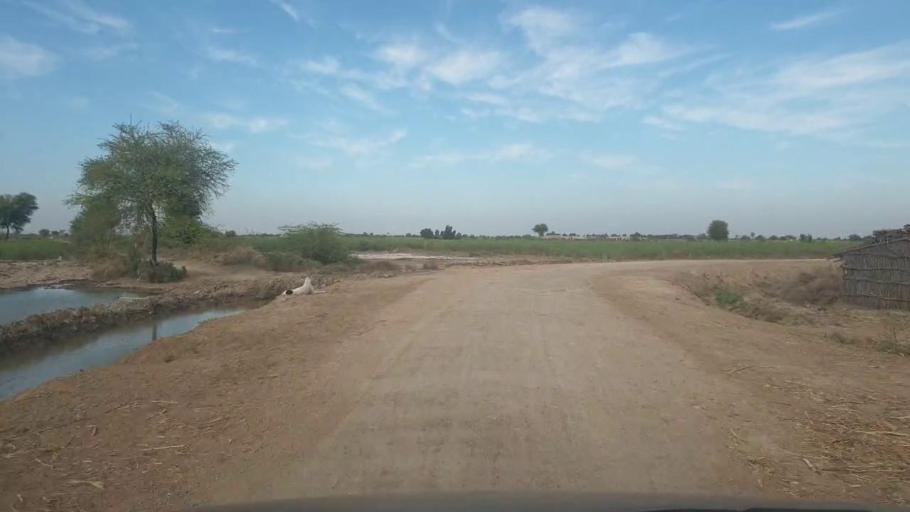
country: PK
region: Sindh
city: Mirwah Gorchani
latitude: 25.3727
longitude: 69.2099
